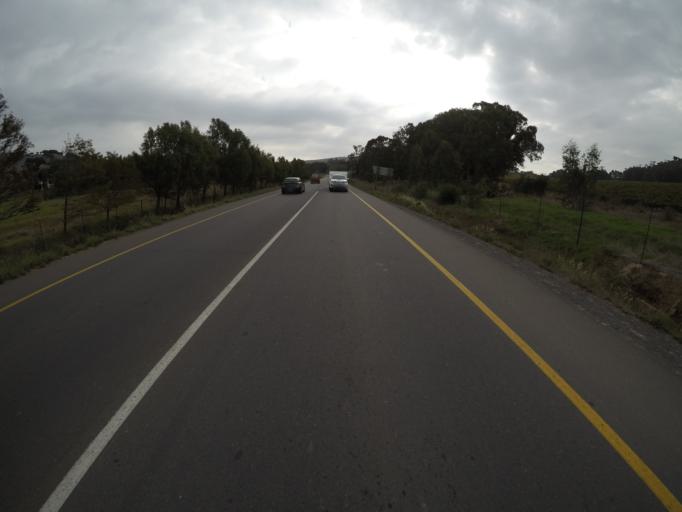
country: ZA
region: Western Cape
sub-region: City of Cape Town
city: Sunset Beach
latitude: -33.8386
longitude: 18.5984
